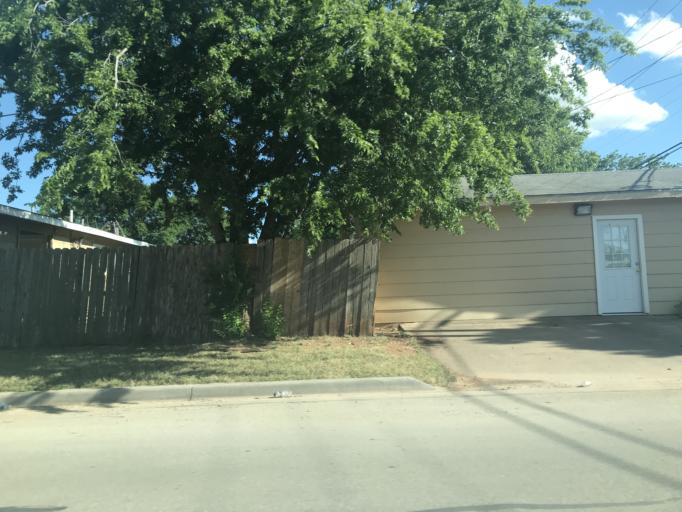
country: US
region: Texas
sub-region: Taylor County
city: Abilene
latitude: 32.4360
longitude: -99.7849
